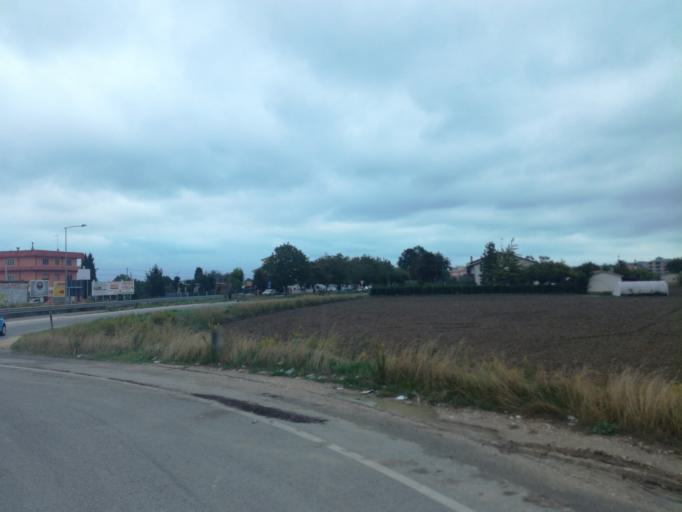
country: IT
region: The Marches
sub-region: Provincia di Ancona
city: Camerata Picena
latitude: 43.5991
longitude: 13.3561
